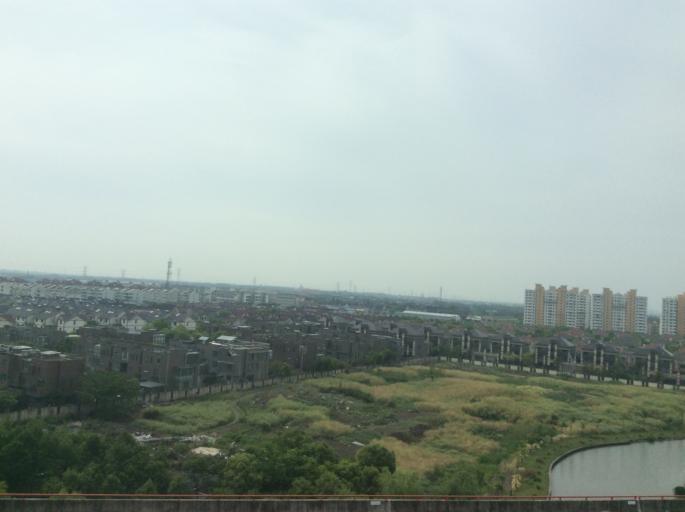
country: CN
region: Shanghai Shi
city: Kangqiao
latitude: 31.1851
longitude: 121.6193
